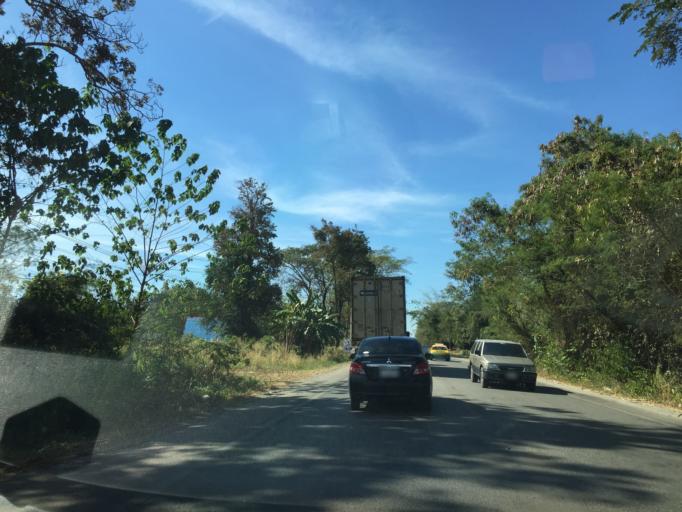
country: TH
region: Changwat Nong Bua Lamphu
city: Na Klang
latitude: 17.3209
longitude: 102.1456
